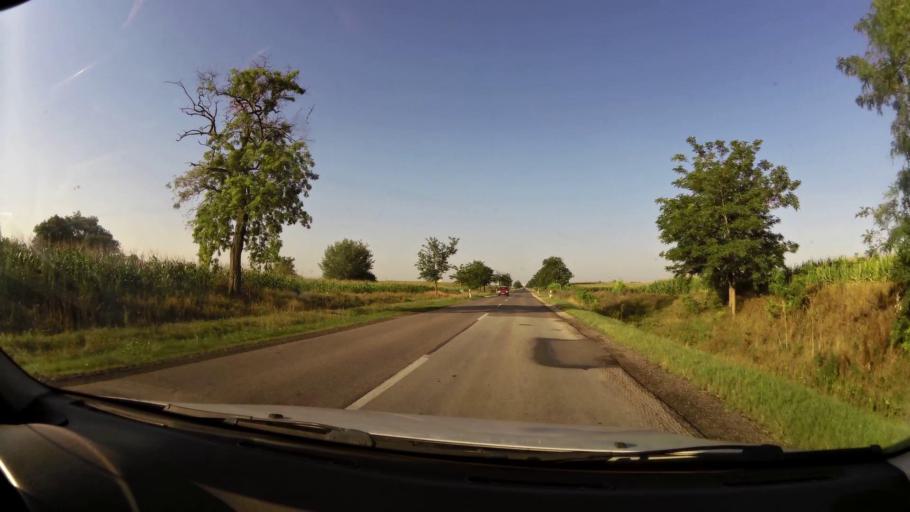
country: HU
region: Pest
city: Cegled
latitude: 47.2076
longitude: 19.8203
